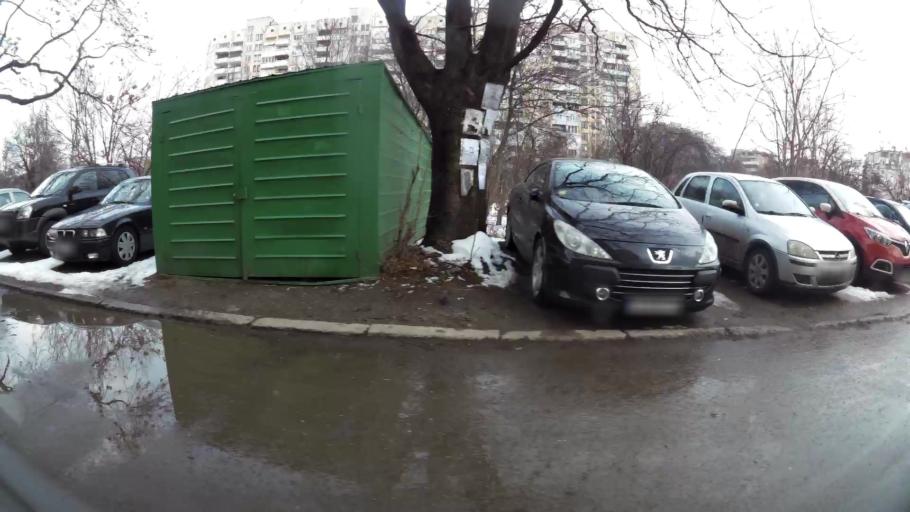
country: BG
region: Sofia-Capital
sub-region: Stolichna Obshtina
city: Sofia
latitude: 42.7007
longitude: 23.3547
